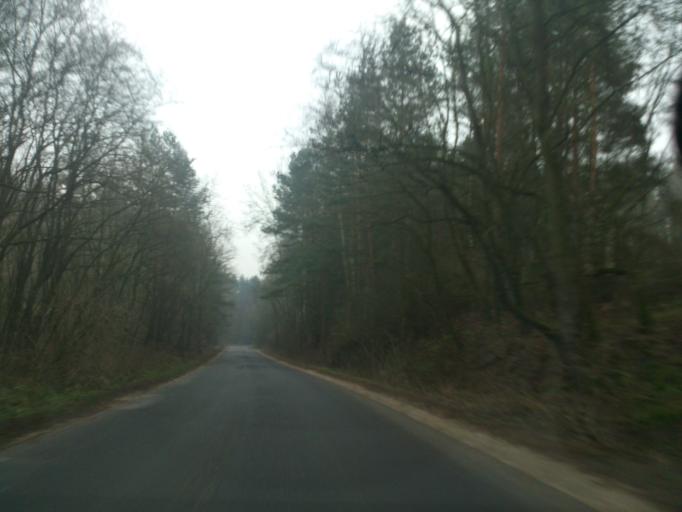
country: PL
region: Kujawsko-Pomorskie
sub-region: Powiat rypinski
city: Wapielsk
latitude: 53.1955
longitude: 19.2364
